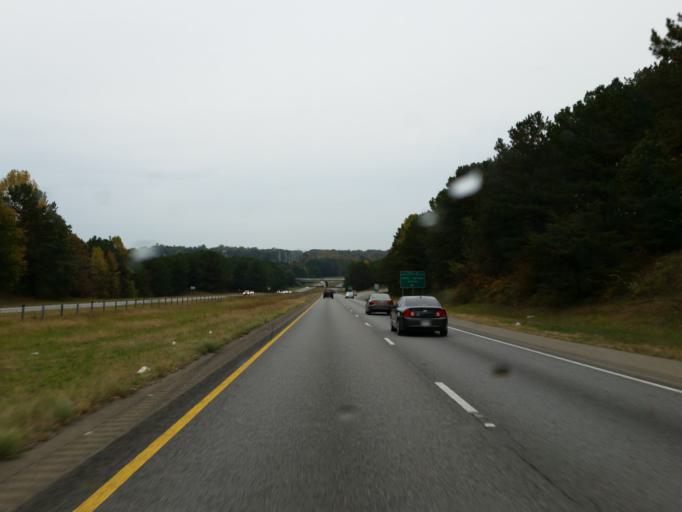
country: US
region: Georgia
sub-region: Cherokee County
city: Holly Springs
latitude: 34.1819
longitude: -84.5069
